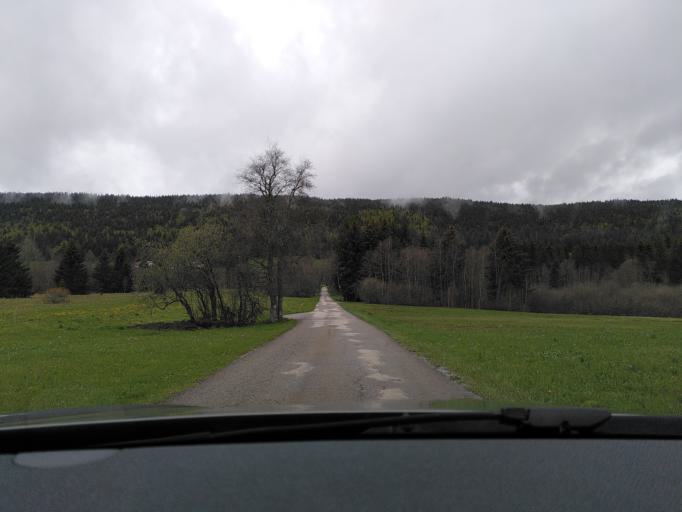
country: FR
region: Franche-Comte
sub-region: Departement du Jura
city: Les Rousses
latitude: 46.5133
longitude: 6.1119
